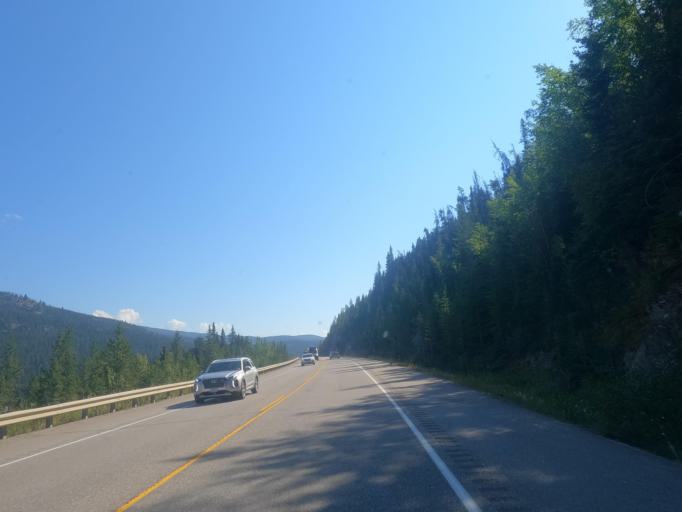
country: CA
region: Alberta
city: Jasper Park Lodge
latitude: 52.8725
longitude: -118.2941
